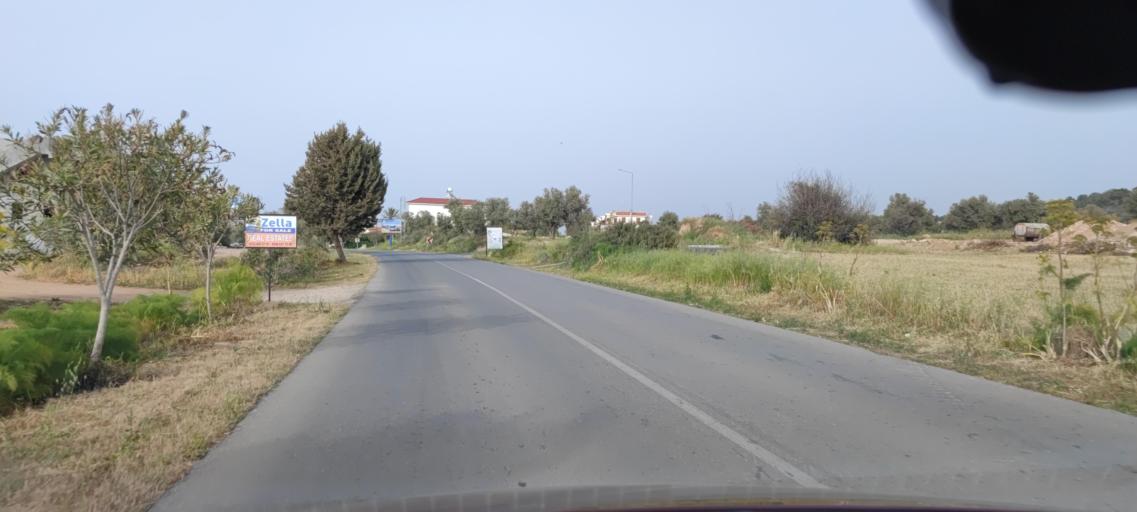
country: CY
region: Ammochostos
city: Leonarisso
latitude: 35.5445
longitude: 34.2001
